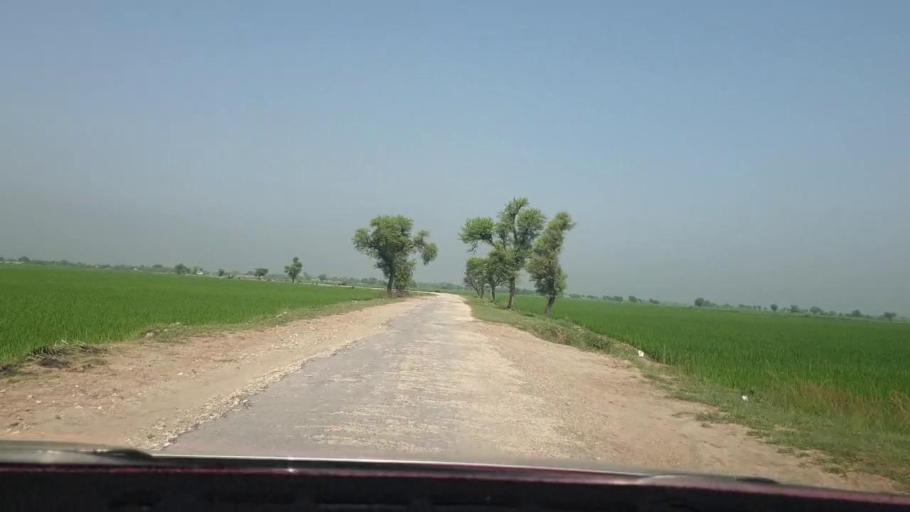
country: PK
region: Sindh
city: Nasirabad
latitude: 27.4295
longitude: 67.9026
